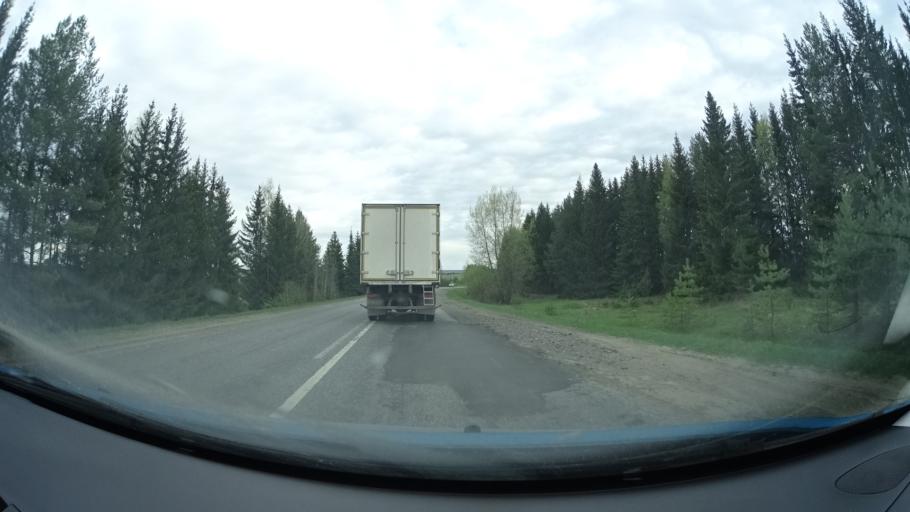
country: RU
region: Perm
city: Yugo-Kamskiy
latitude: 57.5754
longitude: 55.6822
